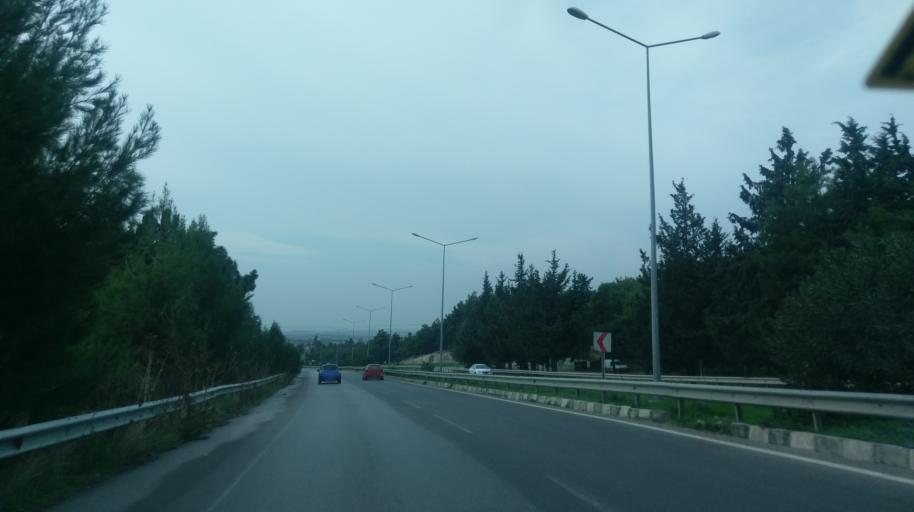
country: CY
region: Keryneia
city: Kyrenia
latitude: 35.2956
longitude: 33.2785
